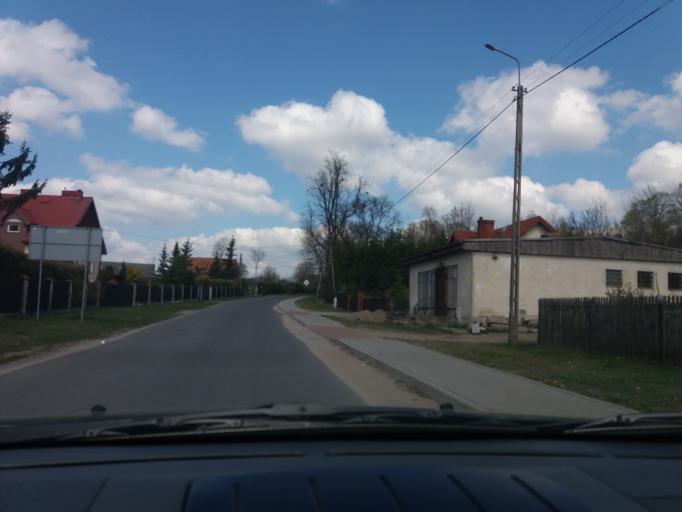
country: PL
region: Warmian-Masurian Voivodeship
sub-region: Powiat nidzicki
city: Nidzica
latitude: 53.3736
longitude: 20.6055
